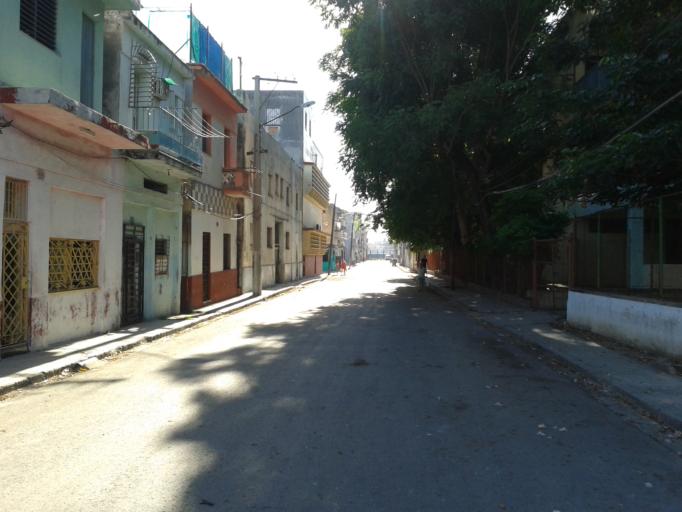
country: CU
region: La Habana
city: Havana
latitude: 23.1246
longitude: -82.3731
